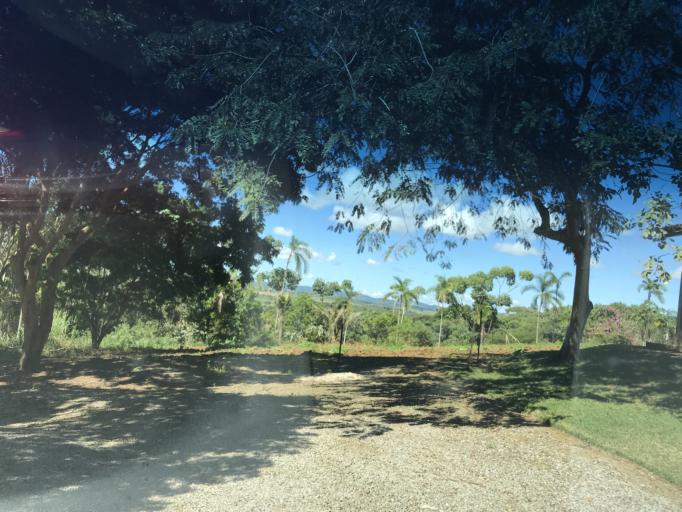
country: BR
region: Bahia
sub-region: Mutuipe
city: Mutuipe
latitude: -13.3731
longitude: -39.3714
